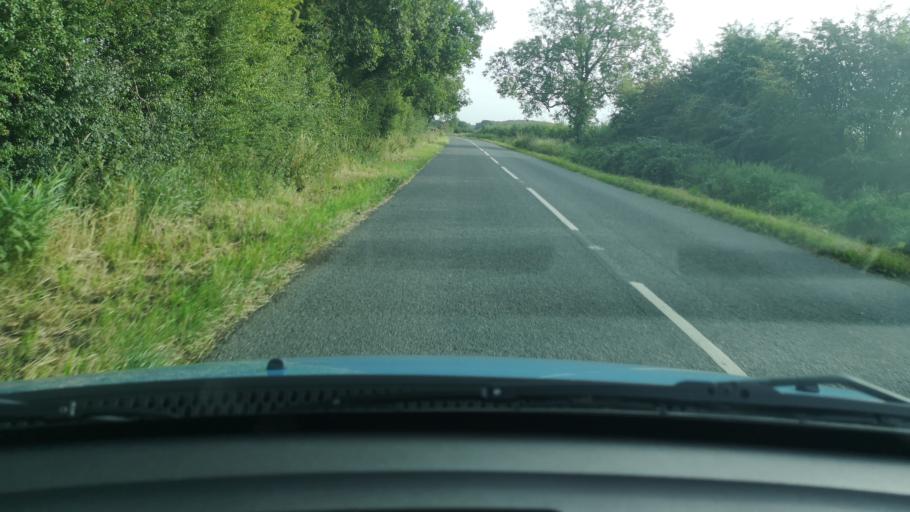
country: GB
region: England
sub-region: Doncaster
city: Moss
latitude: 53.6231
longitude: -1.0726
